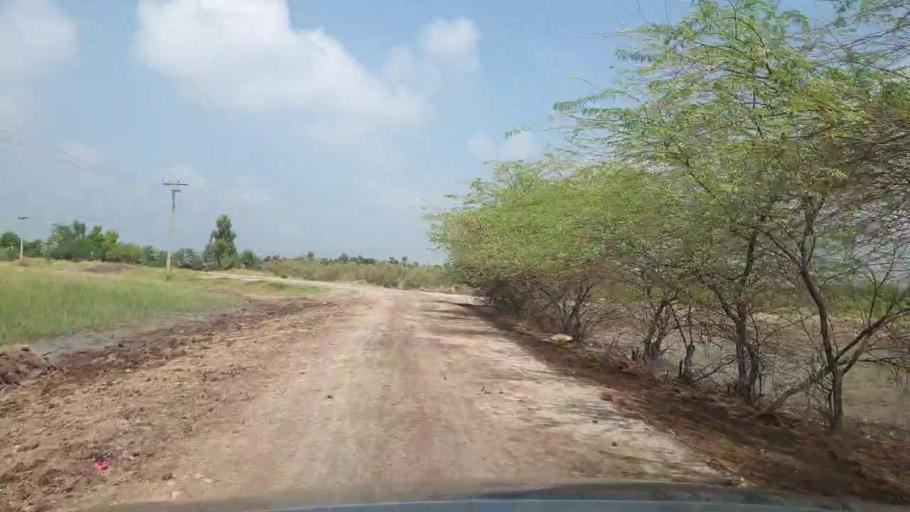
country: PK
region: Sindh
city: Pir jo Goth
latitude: 27.6054
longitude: 68.6965
